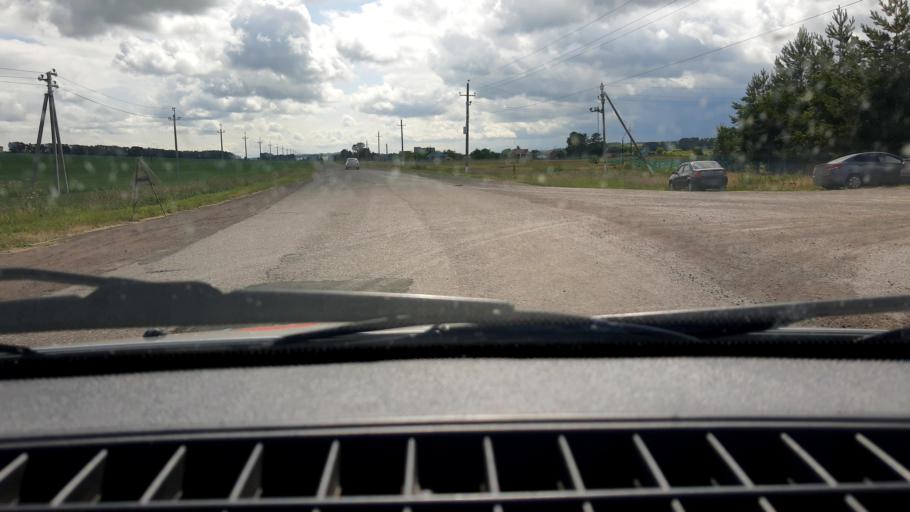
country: RU
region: Bashkortostan
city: Ulukulevo
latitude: 54.4050
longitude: 56.2546
